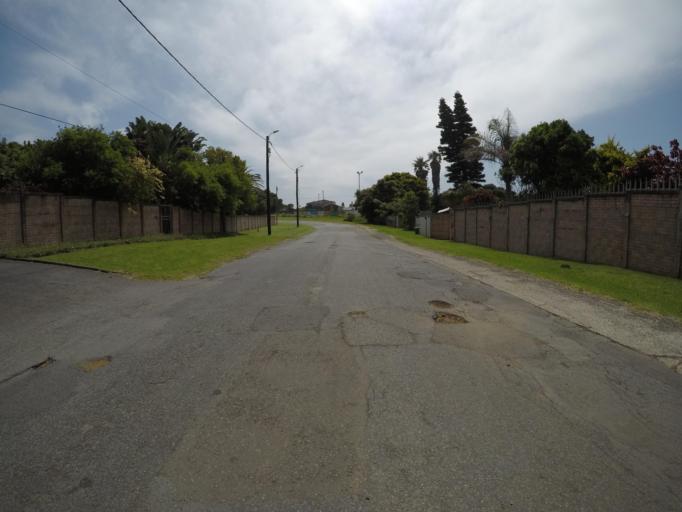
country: ZA
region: Eastern Cape
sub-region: Buffalo City Metropolitan Municipality
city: East London
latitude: -32.9393
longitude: 28.0232
